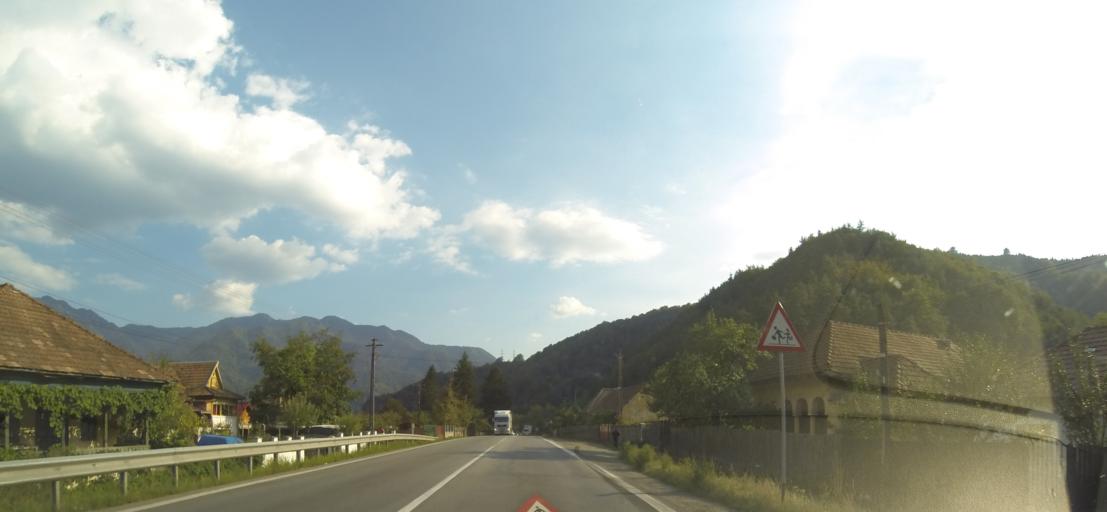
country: RO
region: Valcea
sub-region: Comuna Brezoi
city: Brezoi
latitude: 45.3672
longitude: 24.2911
